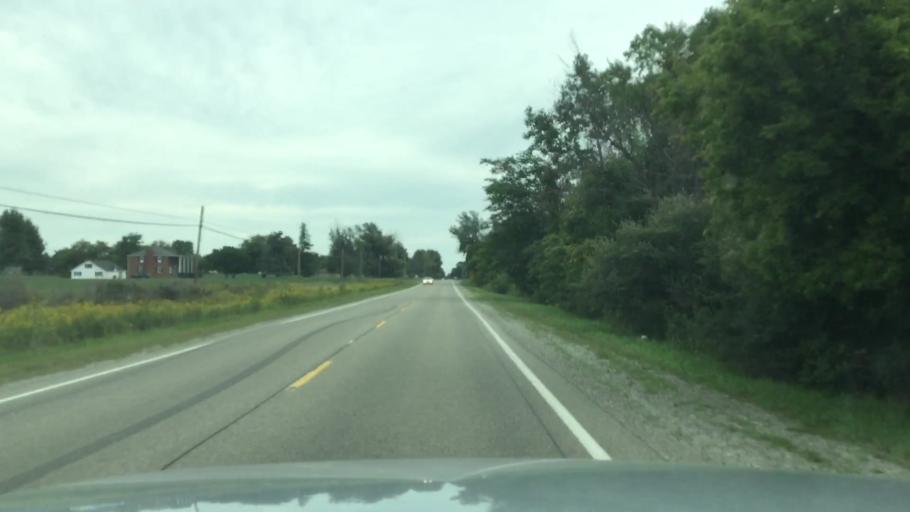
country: US
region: Michigan
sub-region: Genesee County
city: Swartz Creek
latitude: 42.9570
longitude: -83.8766
